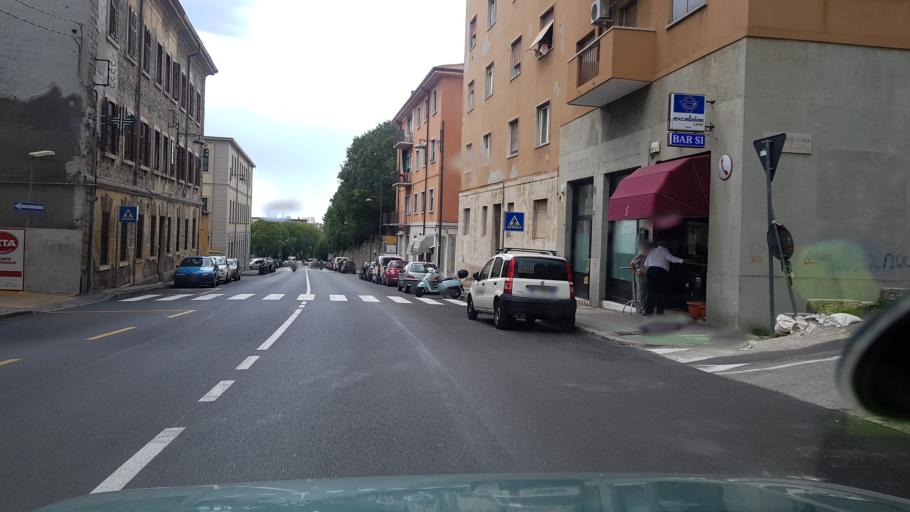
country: IT
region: Friuli Venezia Giulia
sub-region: Provincia di Trieste
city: Trieste
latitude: 45.6422
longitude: 13.7972
